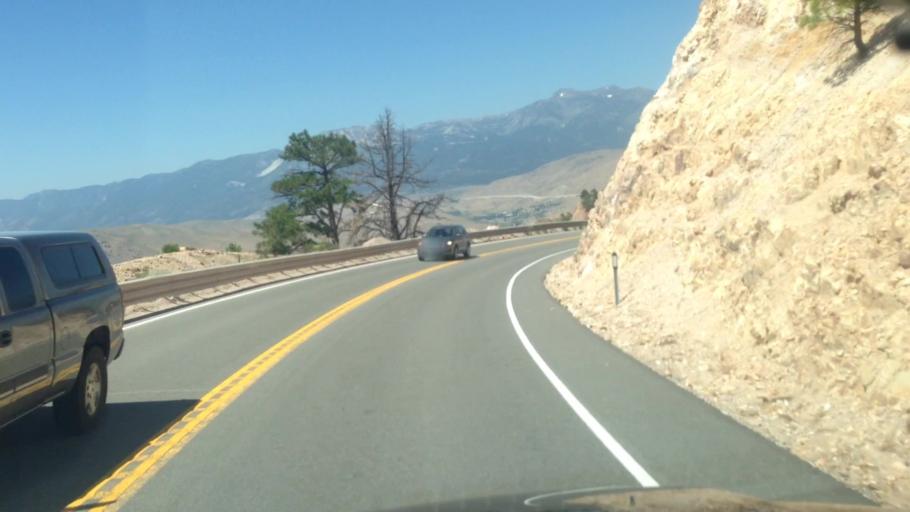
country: US
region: Nevada
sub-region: Storey County
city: Virginia City
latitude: 39.3756
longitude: -119.6883
